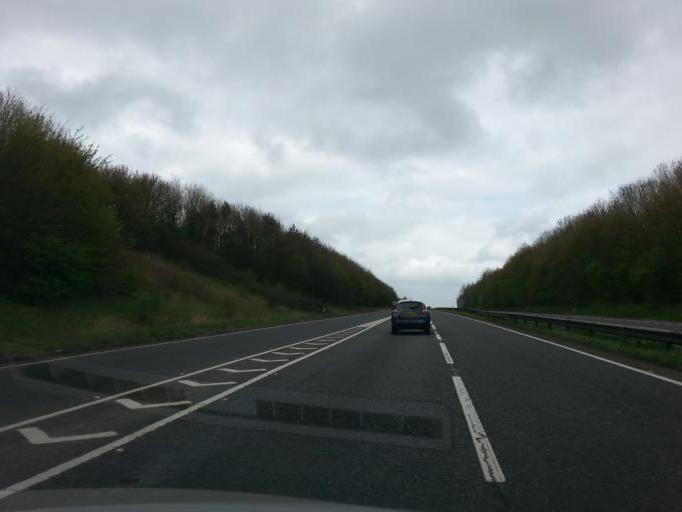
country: GB
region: England
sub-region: Somerset
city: Stoke-sub-Hamdon
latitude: 50.9537
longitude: -2.7667
